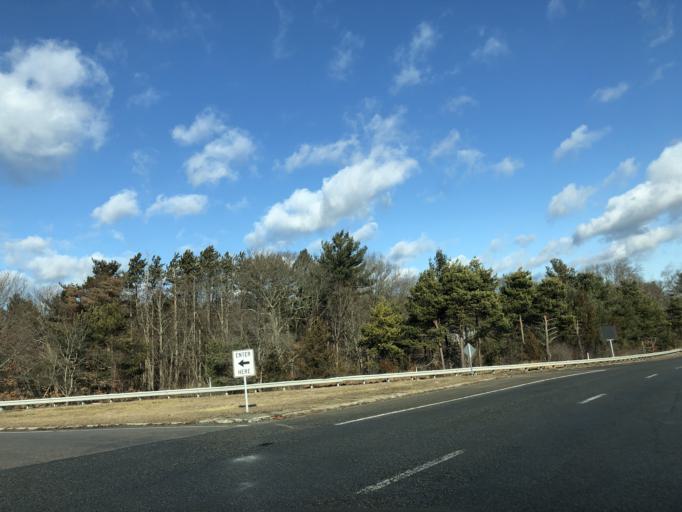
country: US
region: Massachusetts
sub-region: Bristol County
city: Norton Center
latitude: 41.9832
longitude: -71.1591
